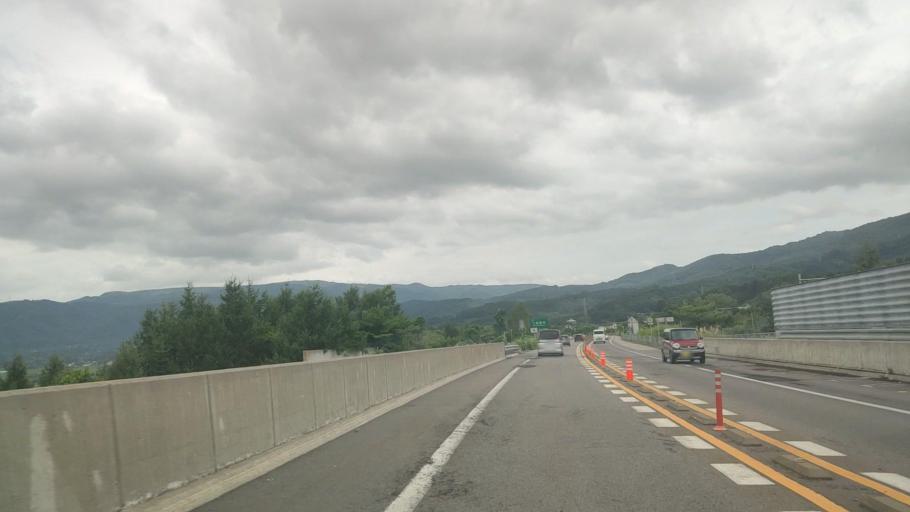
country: JP
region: Hokkaido
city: Nanae
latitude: 41.9175
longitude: 140.6829
